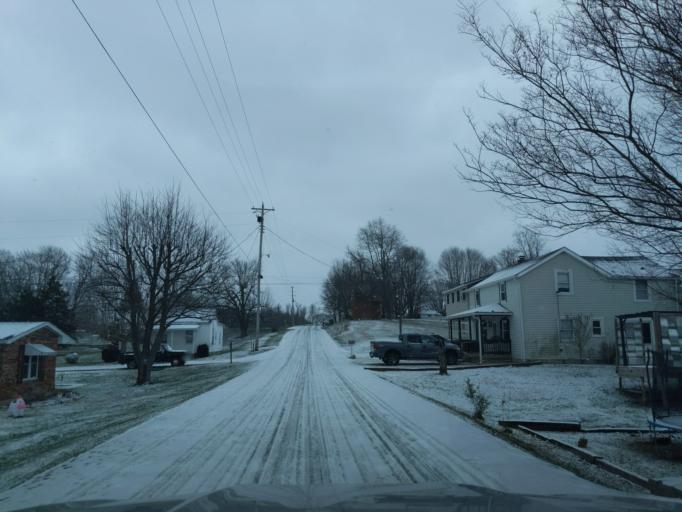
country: US
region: Indiana
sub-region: Decatur County
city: Greensburg
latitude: 39.2101
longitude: -85.4344
